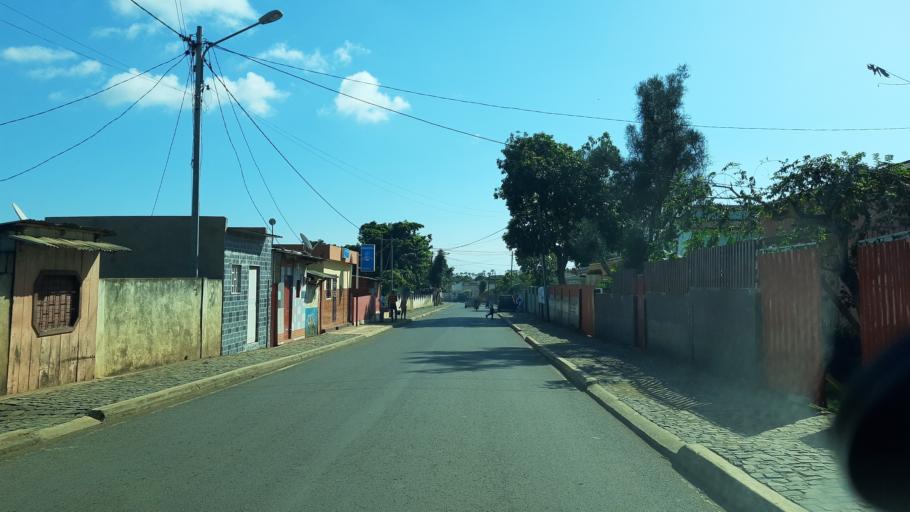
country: ST
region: Sao Tome Island
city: Sao Tome
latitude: 0.3292
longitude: 6.7297
